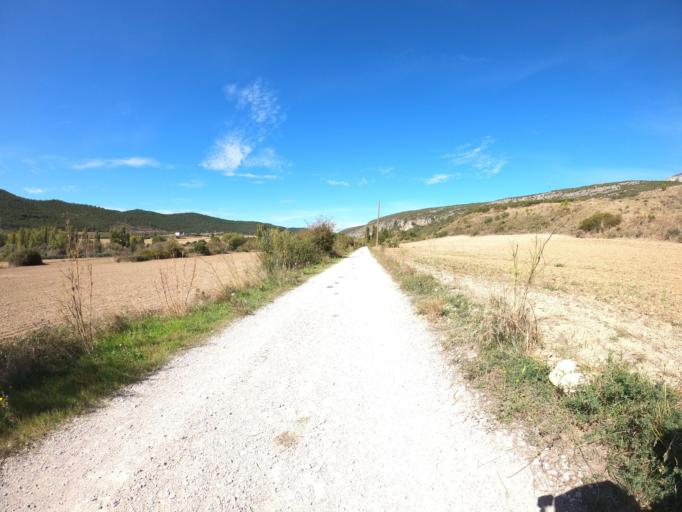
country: ES
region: Navarre
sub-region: Provincia de Navarra
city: Liedena
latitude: 42.6191
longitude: -1.2866
